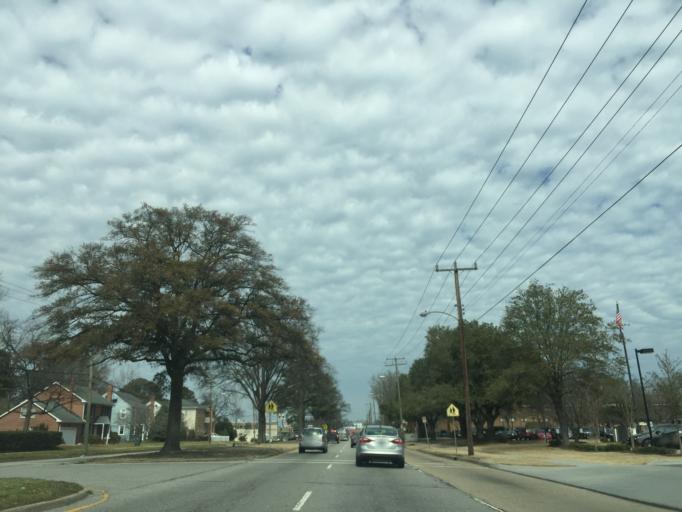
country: US
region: Virginia
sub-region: City of Norfolk
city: Norfolk
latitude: 36.9108
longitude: -76.2743
